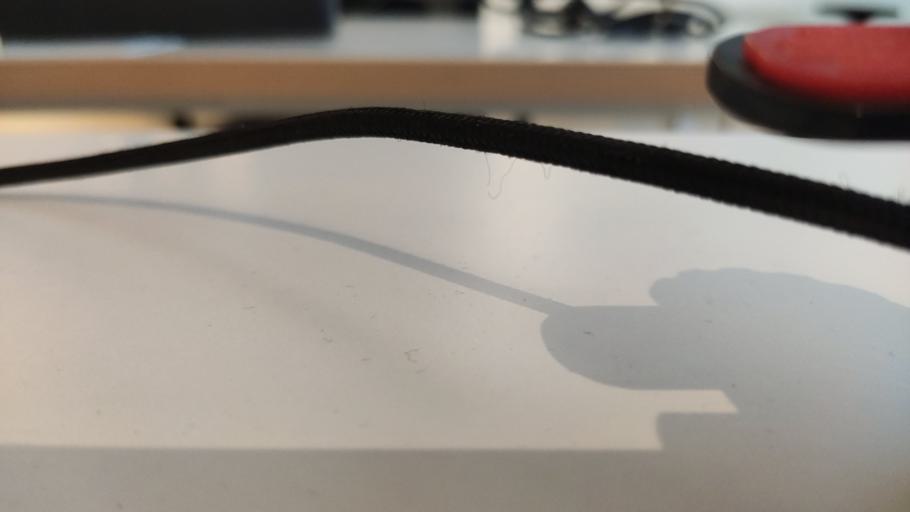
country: RU
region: Moskovskaya
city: Novopetrovskoye
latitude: 55.9111
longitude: 36.4419
